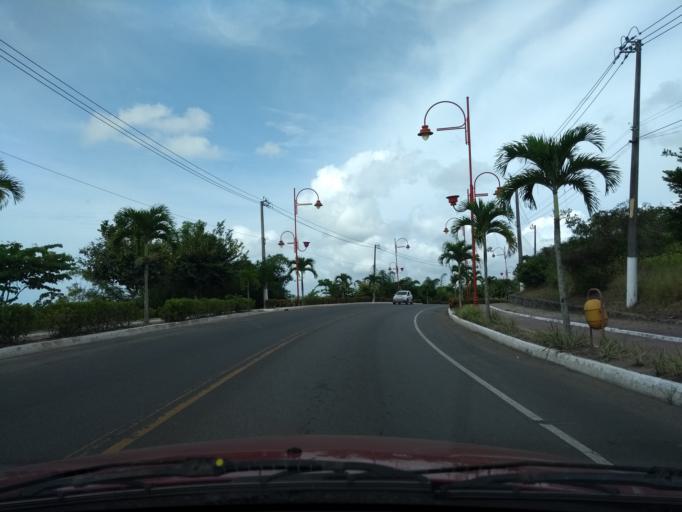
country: BR
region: Bahia
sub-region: Sao Francisco Do Conde
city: Sao Francisco do Conde
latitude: -12.6150
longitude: -38.6572
